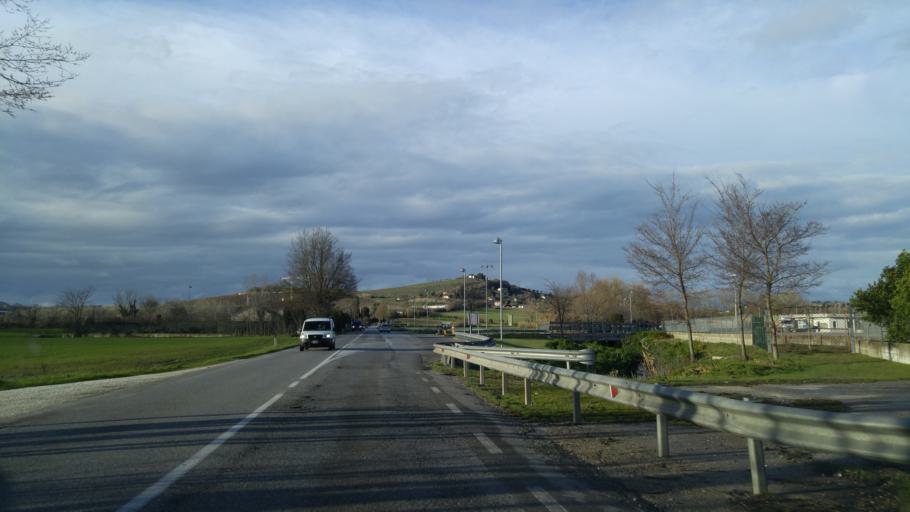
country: IT
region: The Marches
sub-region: Provincia di Ancona
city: Camerano
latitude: 43.5267
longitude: 13.5307
